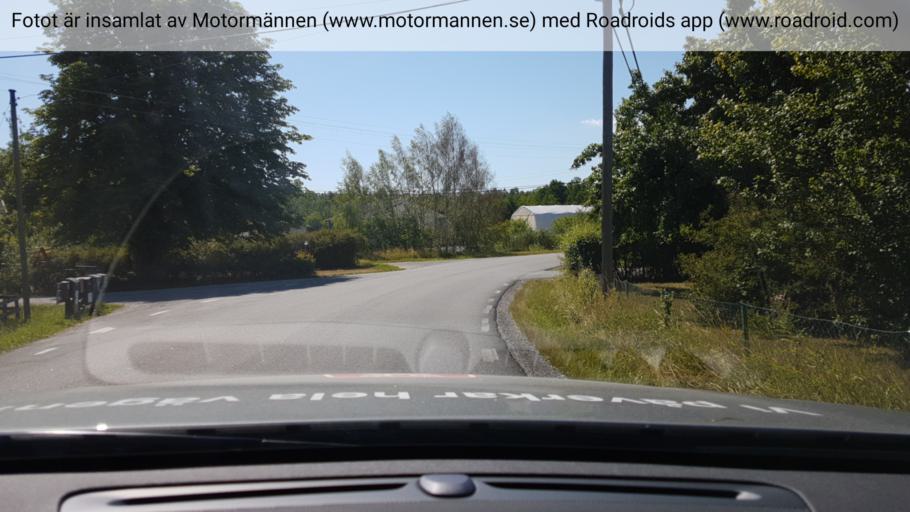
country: SE
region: Stockholm
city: Stenhamra
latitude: 59.4100
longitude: 17.6755
